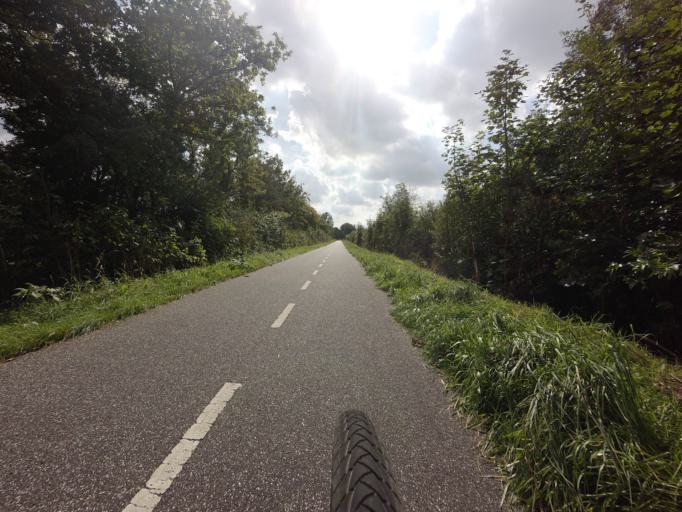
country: DK
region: Central Jutland
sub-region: Herning Kommune
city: Sunds
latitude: 56.1794
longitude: 9.0050
